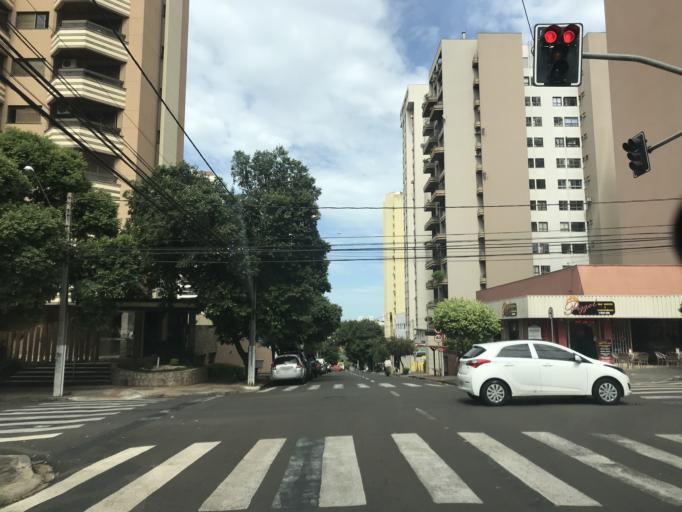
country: BR
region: Parana
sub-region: Londrina
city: Londrina
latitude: -23.3144
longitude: -51.1678
